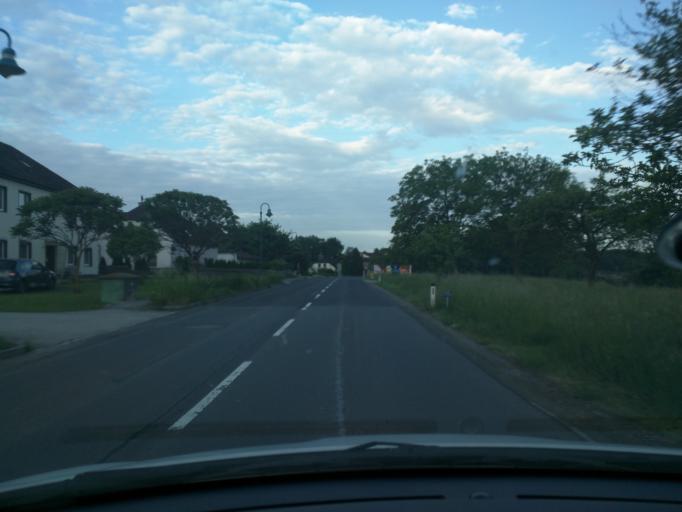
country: AT
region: Lower Austria
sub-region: Politischer Bezirk Amstetten
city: Zeillern
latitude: 48.1216
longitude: 14.8126
